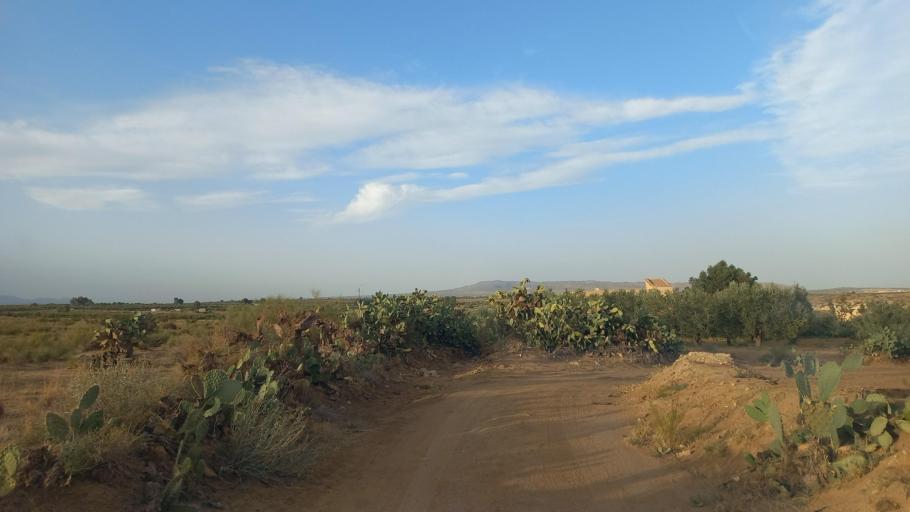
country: TN
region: Al Qasrayn
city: Kasserine
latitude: 35.2153
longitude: 9.0601
